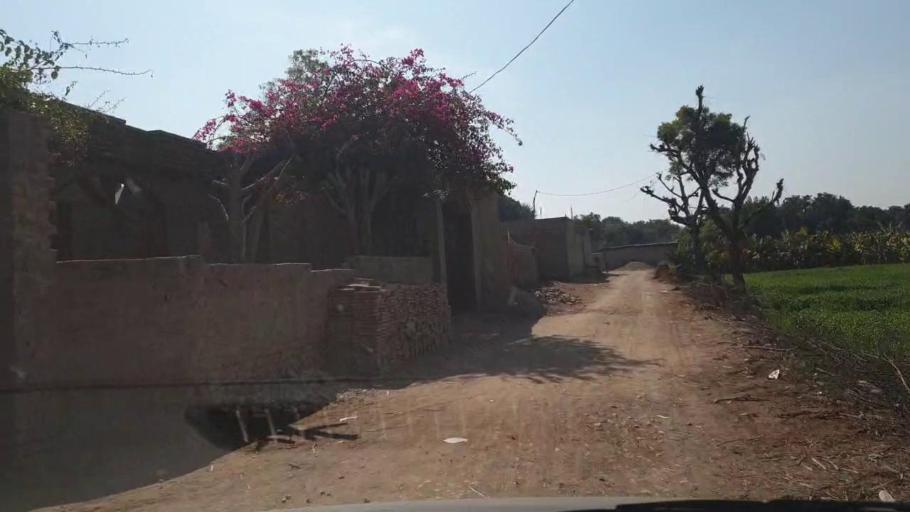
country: PK
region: Sindh
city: Tando Allahyar
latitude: 25.3891
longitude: 68.7808
